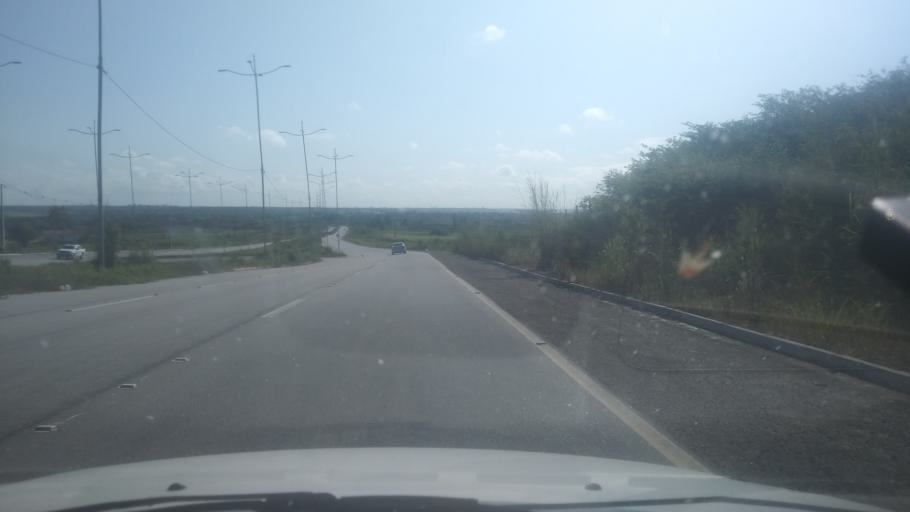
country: BR
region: Rio Grande do Norte
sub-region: Macaiba
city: Macaiba
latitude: -5.8217
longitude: -35.3676
